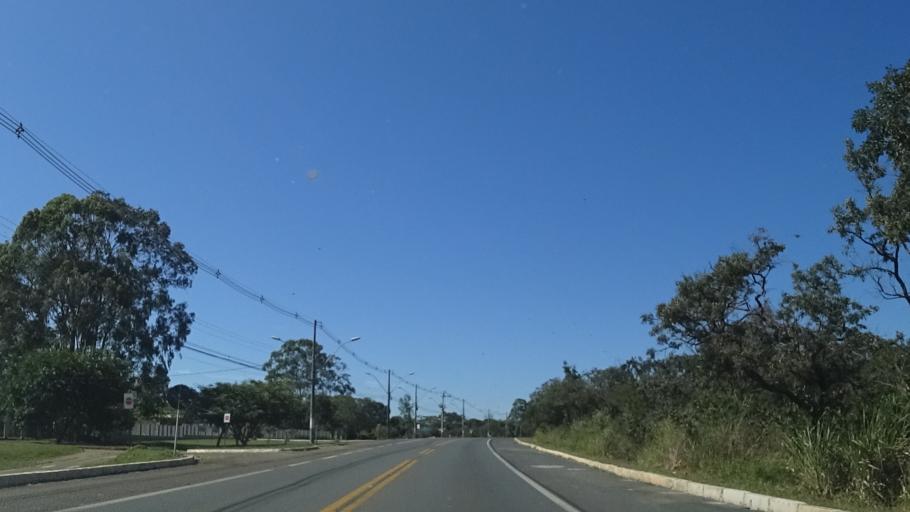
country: BR
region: Federal District
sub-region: Brasilia
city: Brasilia
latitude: -15.8841
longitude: -47.9574
